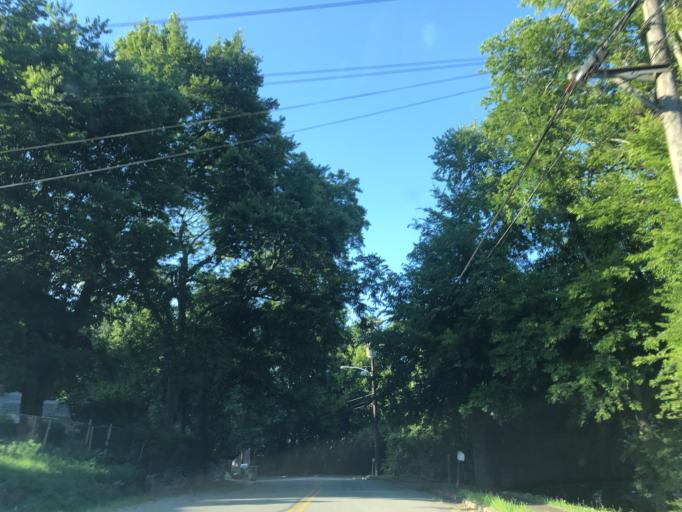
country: US
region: Tennessee
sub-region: Davidson County
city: Nashville
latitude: 36.1898
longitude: -86.8307
